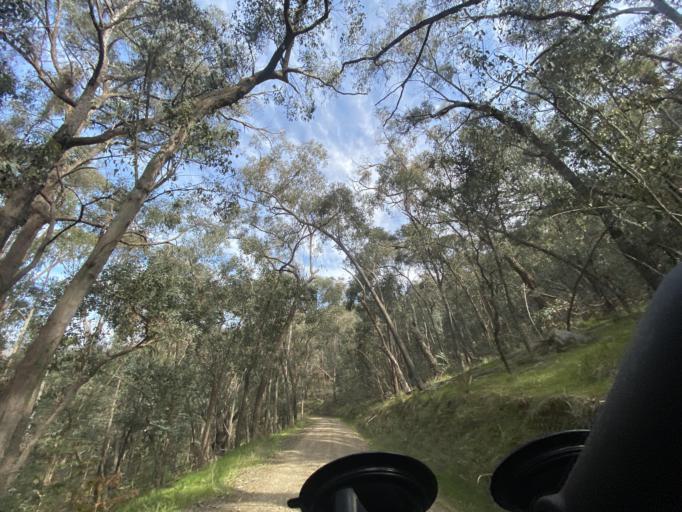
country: AU
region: Victoria
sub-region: Mansfield
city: Mansfield
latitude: -36.7981
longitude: 146.1140
